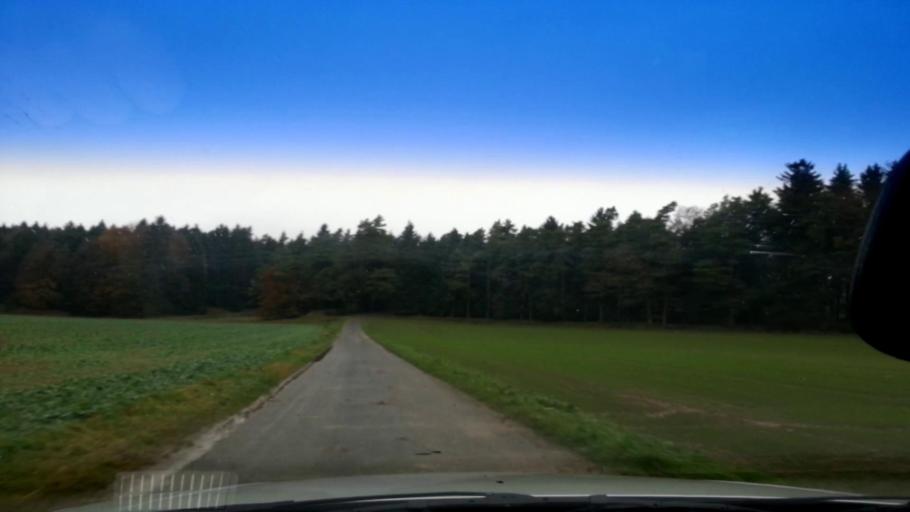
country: DE
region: Bavaria
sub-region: Upper Franconia
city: Wattendorf
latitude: 50.0159
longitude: 11.1484
